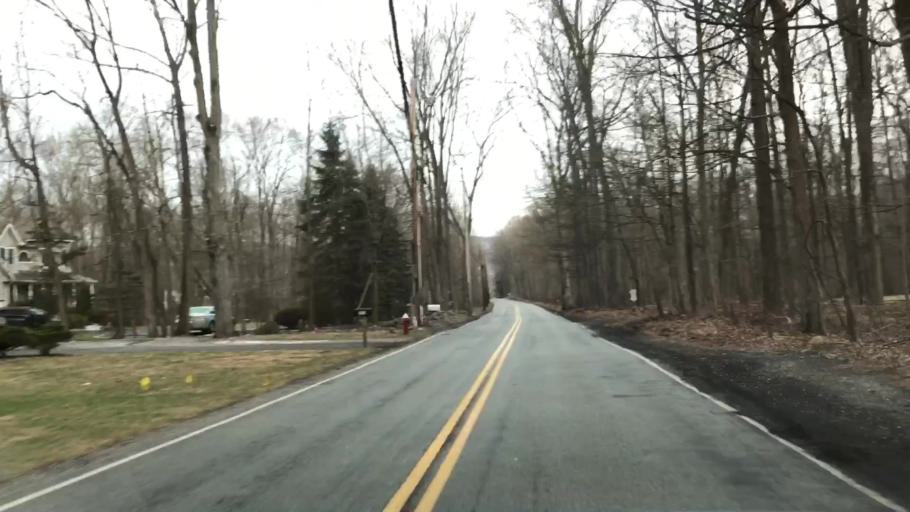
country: US
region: New York
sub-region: Rockland County
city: Viola
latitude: 41.1388
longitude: -74.0972
